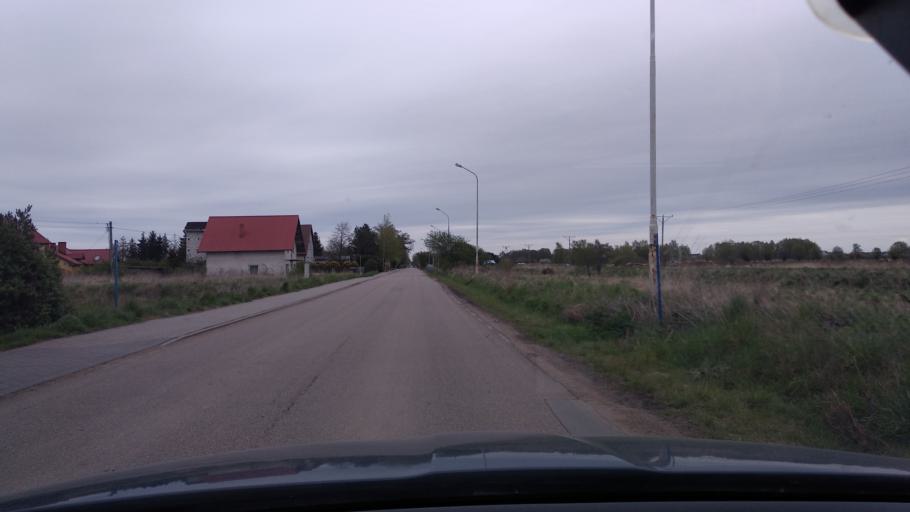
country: PL
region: Pomeranian Voivodeship
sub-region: Powiat gdanski
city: Pruszcz Gdanski
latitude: 54.2771
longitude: 18.6637
